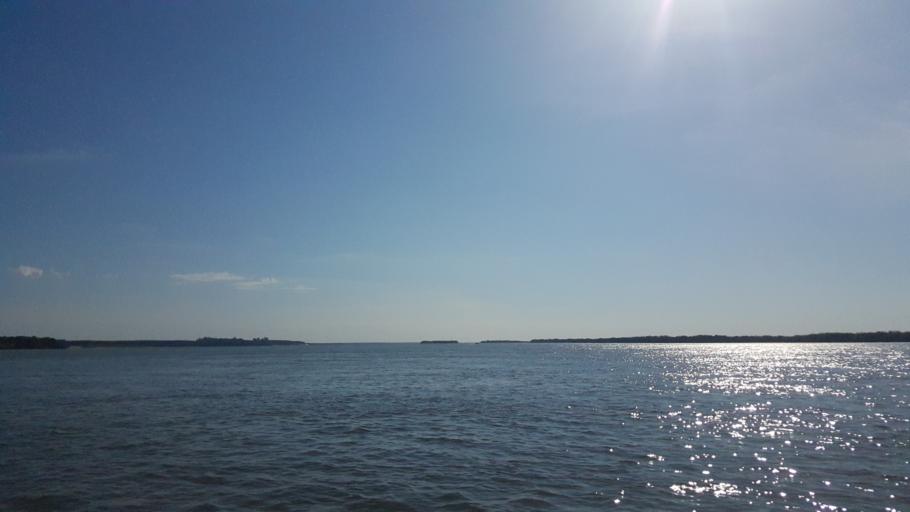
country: AR
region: Corrientes
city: Ituzaingo
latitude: -27.6060
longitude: -56.8230
